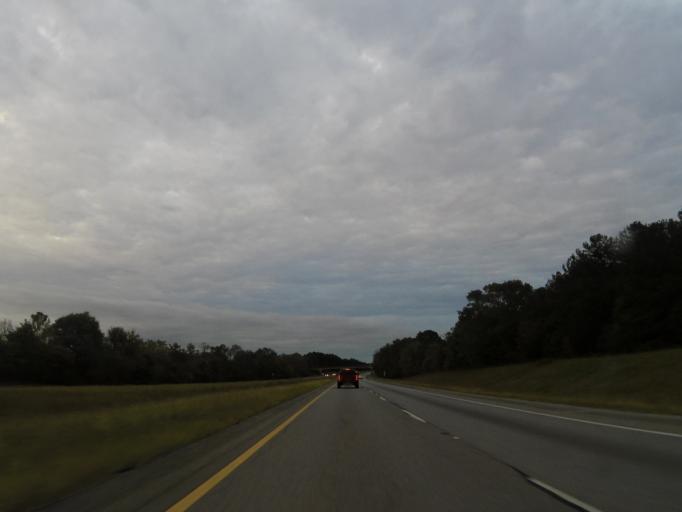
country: US
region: Alabama
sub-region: Saint Clair County
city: Ashville
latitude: 33.8864
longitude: -86.2528
